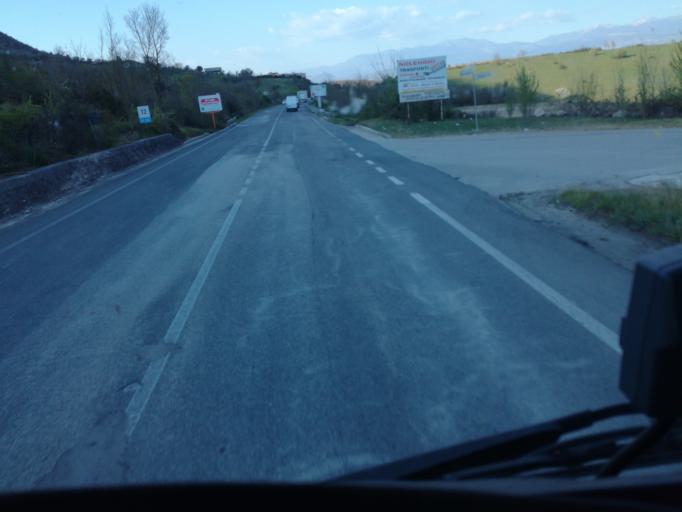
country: IT
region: Latium
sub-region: Provincia di Frosinone
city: Giuliano di Roma
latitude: 41.5682
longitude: 13.2681
